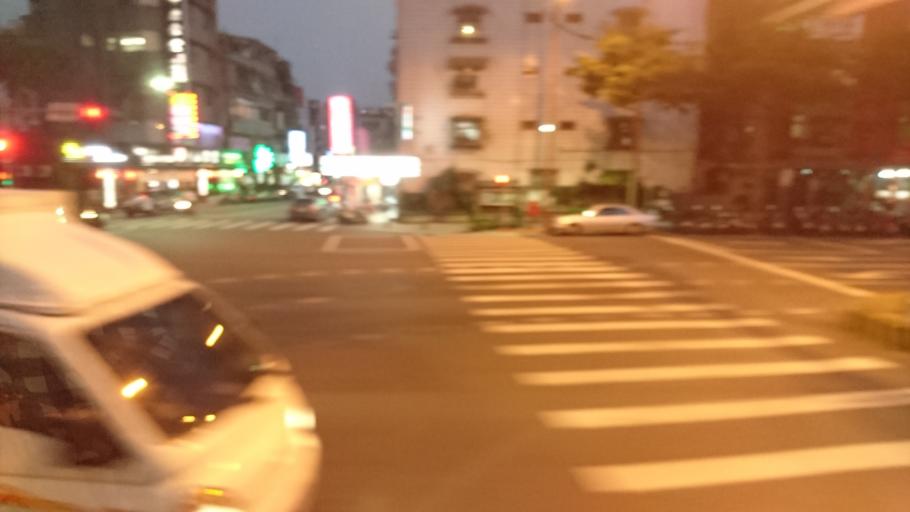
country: TW
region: Taipei
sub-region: Taipei
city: Banqiao
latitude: 25.0318
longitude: 121.4947
